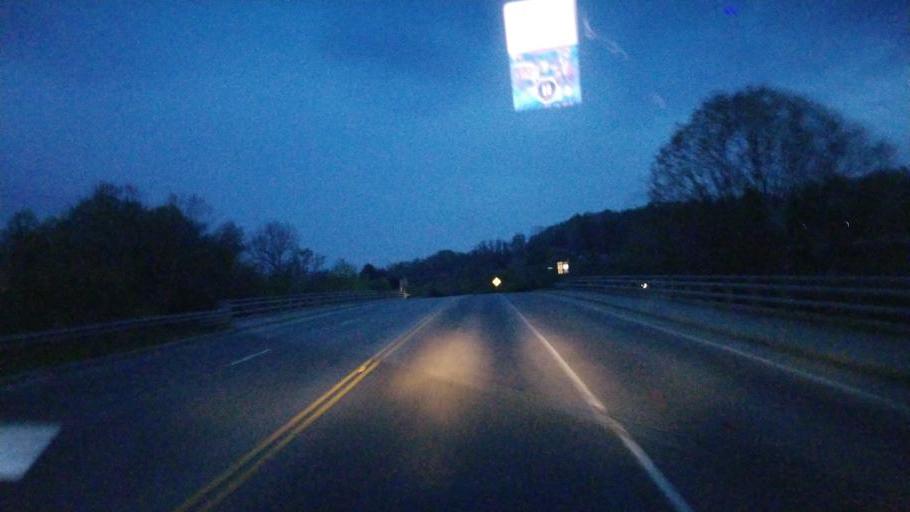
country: US
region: Virginia
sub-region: Smyth County
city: Marion
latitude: 36.8507
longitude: -81.4859
